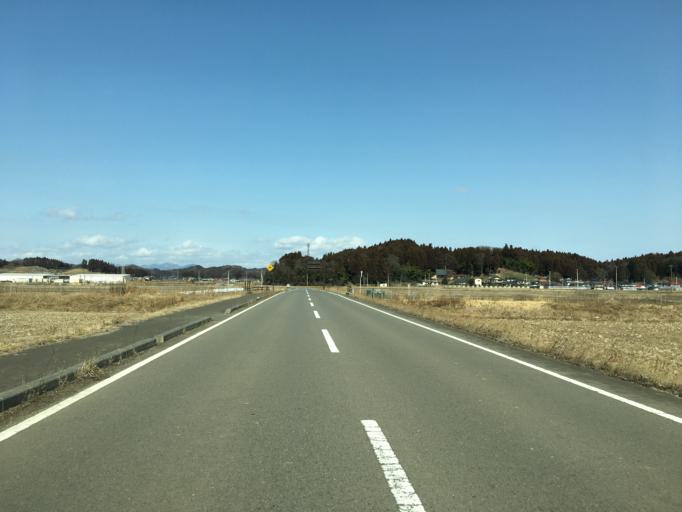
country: JP
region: Fukushima
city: Ishikawa
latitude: 37.1172
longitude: 140.2774
